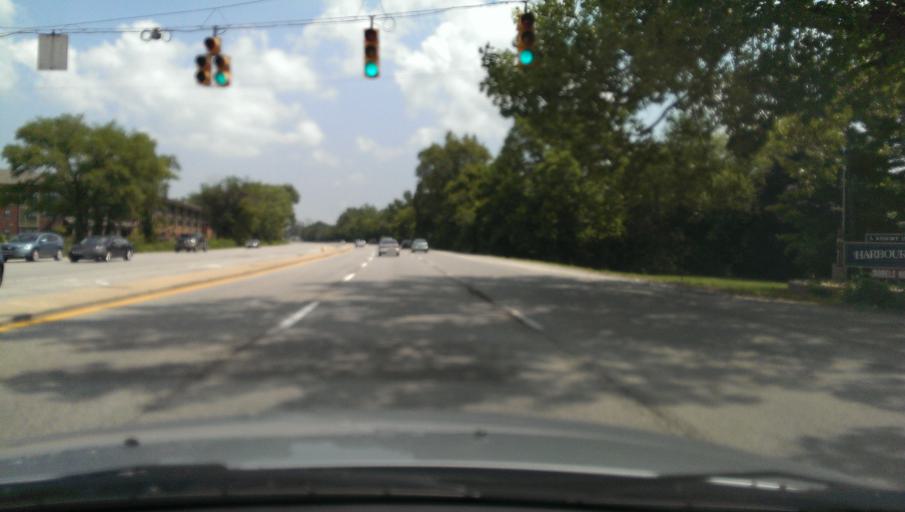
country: US
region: Indiana
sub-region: Marion County
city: Broad Ripple
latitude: 39.8362
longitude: -86.1188
